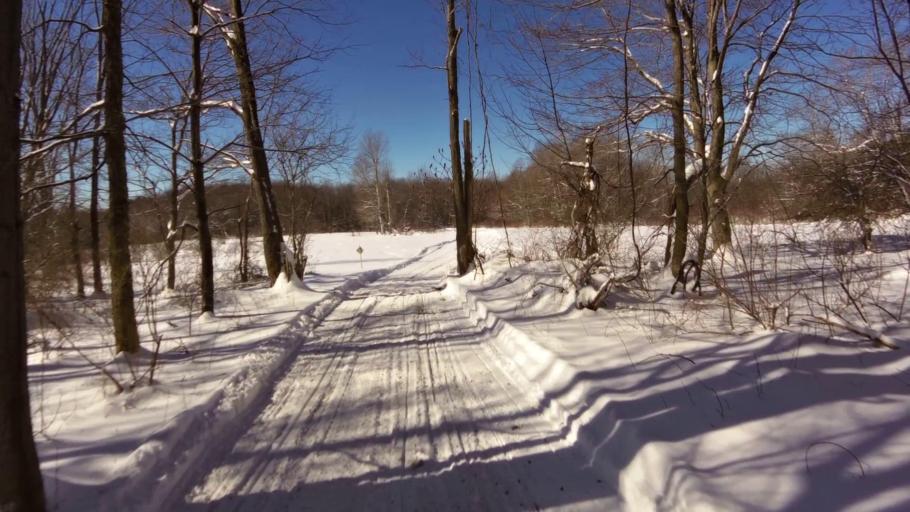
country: US
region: New York
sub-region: Chautauqua County
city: Mayville
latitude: 42.2234
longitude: -79.3988
